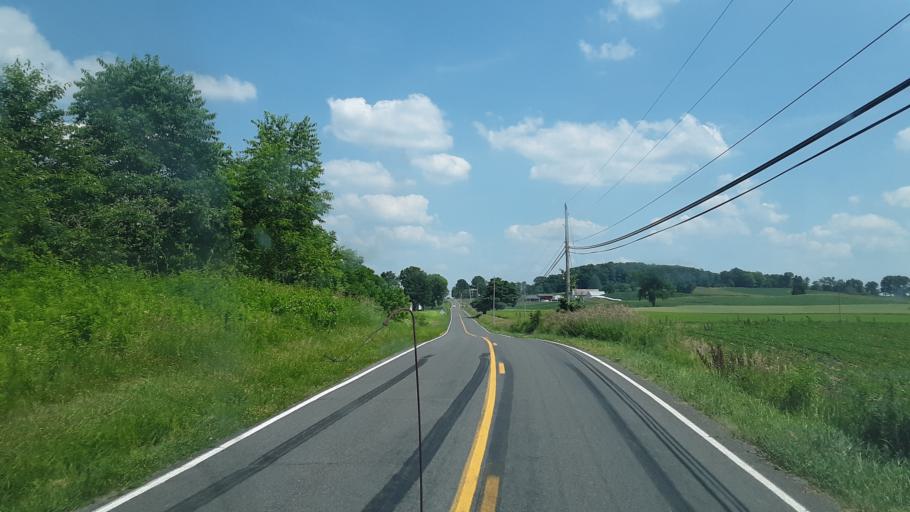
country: US
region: Ohio
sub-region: Stark County
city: Navarre
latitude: 40.7022
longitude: -81.4888
